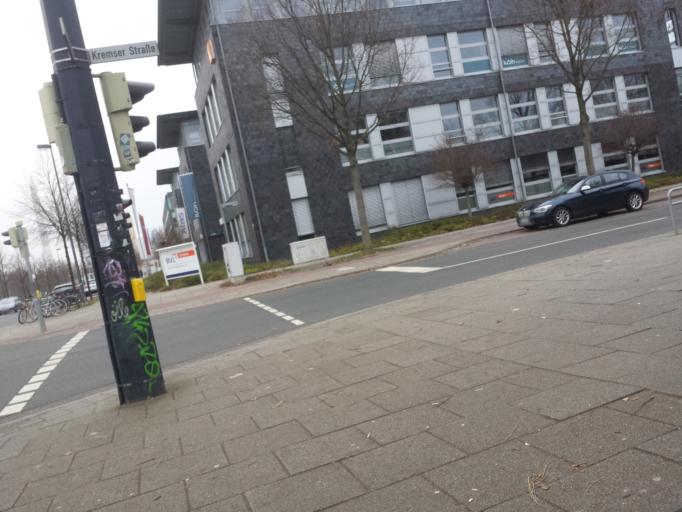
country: DE
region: Bremen
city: Bremen
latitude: 53.1028
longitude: 8.8596
